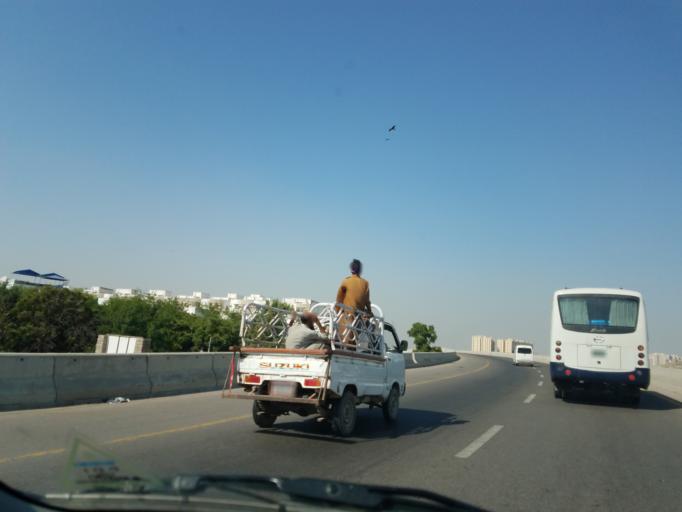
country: PK
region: Sindh
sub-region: Karachi District
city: Karachi
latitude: 24.9146
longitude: 67.0780
